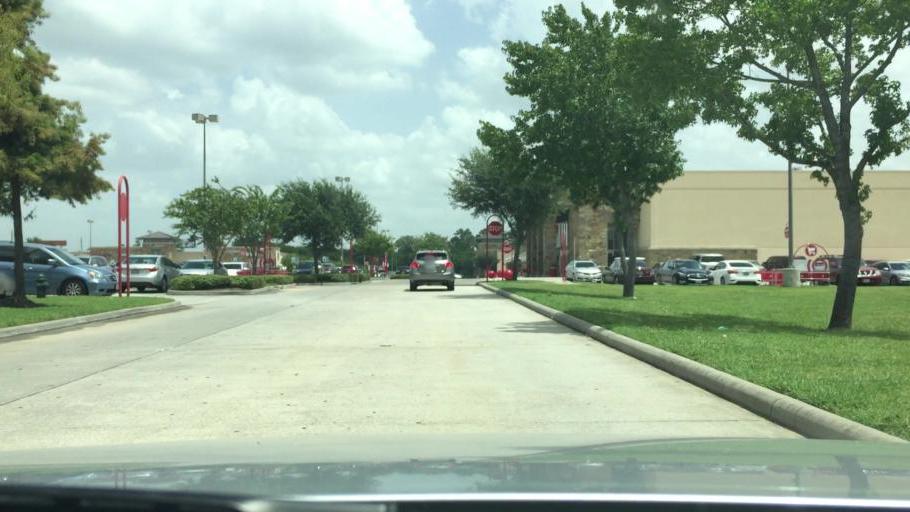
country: US
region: Texas
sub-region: Harris County
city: Hudson
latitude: 29.9676
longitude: -95.5321
